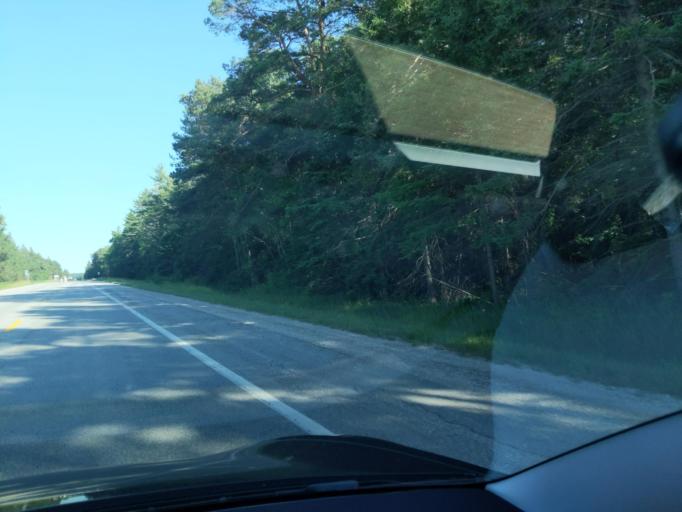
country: US
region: Michigan
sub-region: Mackinac County
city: Saint Ignace
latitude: 45.7598
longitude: -84.7077
